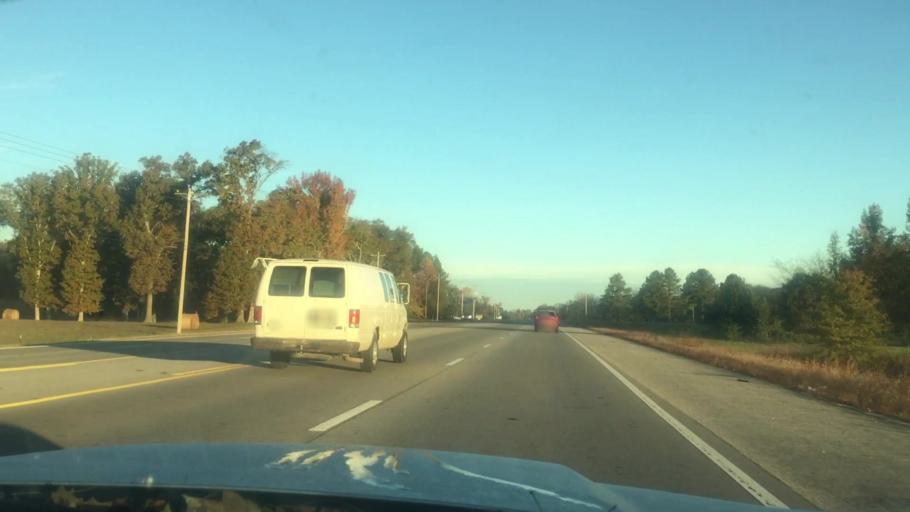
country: US
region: Tennessee
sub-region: Franklin County
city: Decherd
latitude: 35.2331
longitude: -86.1100
